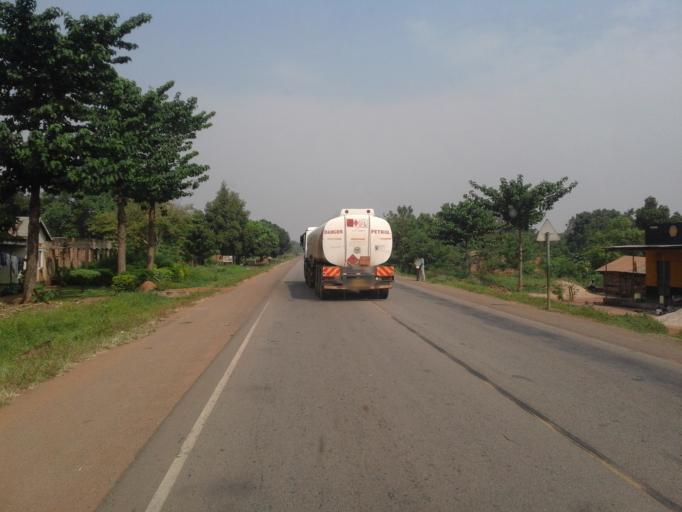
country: UG
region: Eastern Region
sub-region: Bugiri District
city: Bugiri
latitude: 0.5771
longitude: 33.7407
